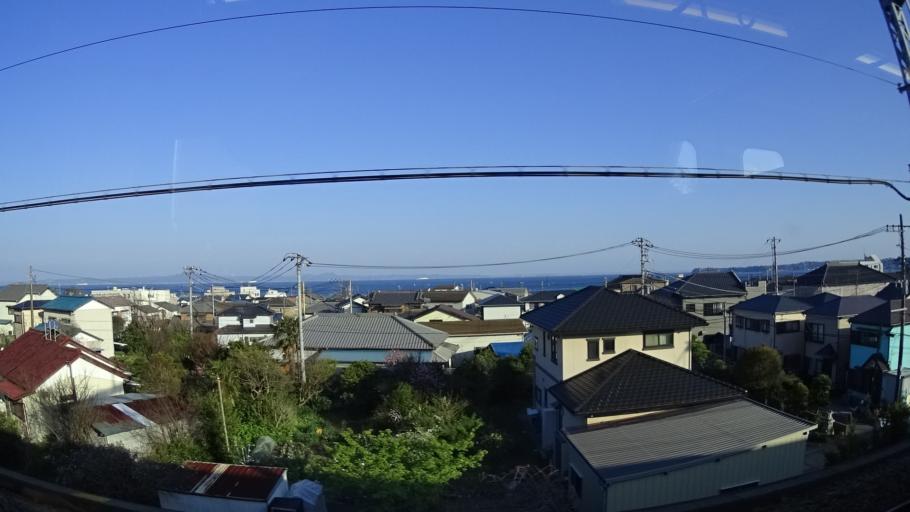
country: JP
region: Kanagawa
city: Miura
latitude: 35.1923
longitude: 139.6582
